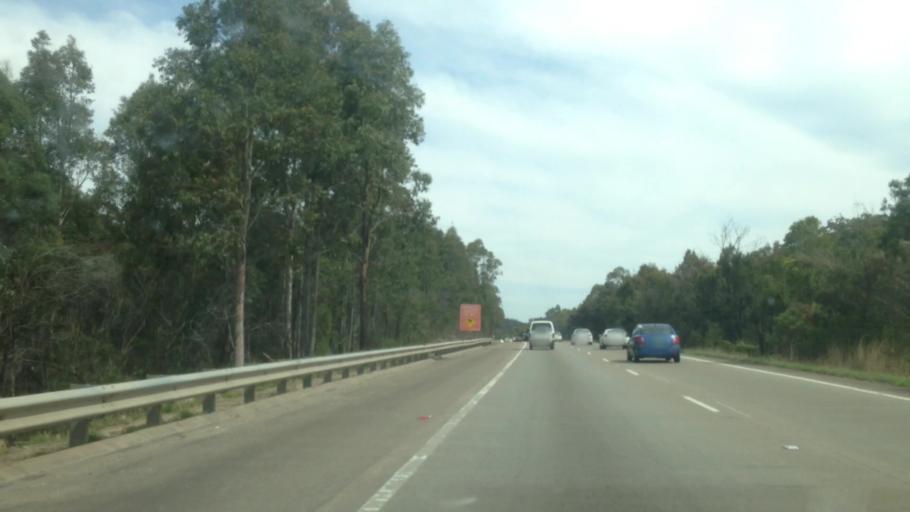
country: AU
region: New South Wales
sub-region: Lake Macquarie Shire
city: Fennell Bay
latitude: -32.9606
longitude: 151.5406
